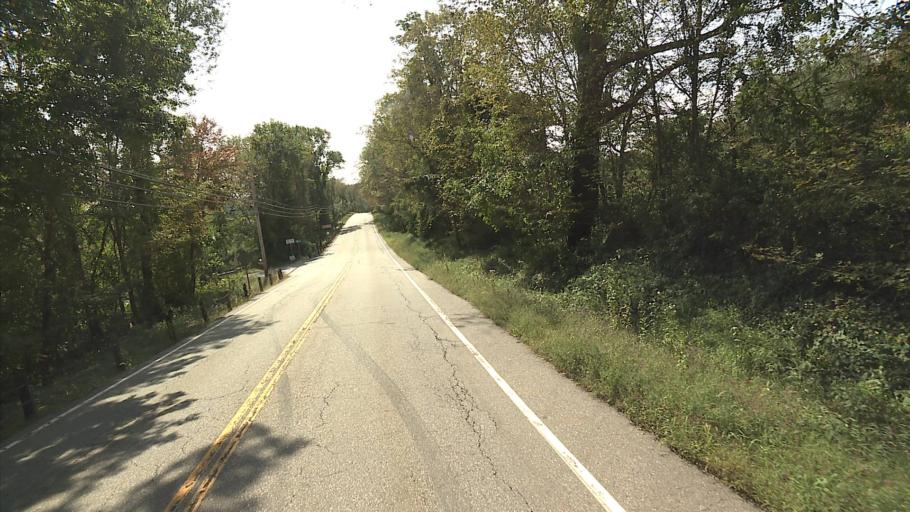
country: US
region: Connecticut
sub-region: Windham County
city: Putnam
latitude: 41.8664
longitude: -71.9602
